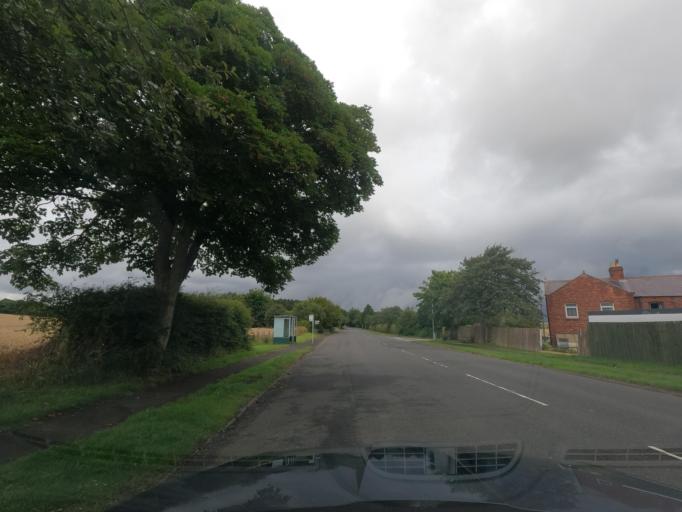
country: GB
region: England
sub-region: Northumberland
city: Ancroft
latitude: 55.7390
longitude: -1.9930
